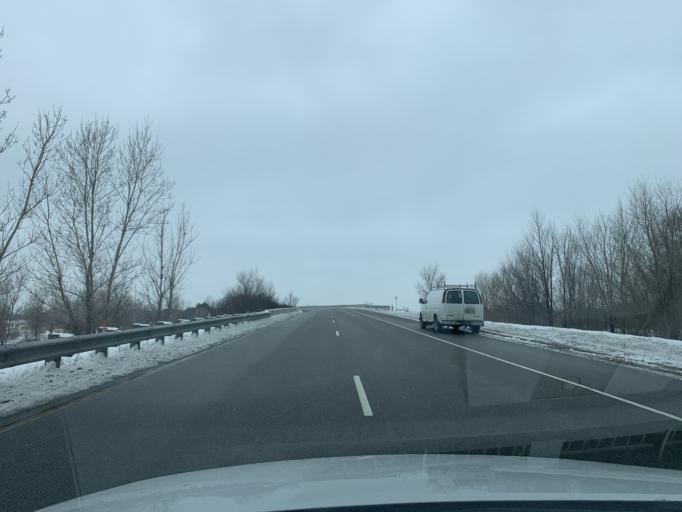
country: US
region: Minnesota
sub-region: Anoka County
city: Coon Rapids
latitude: 45.1239
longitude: -93.3042
